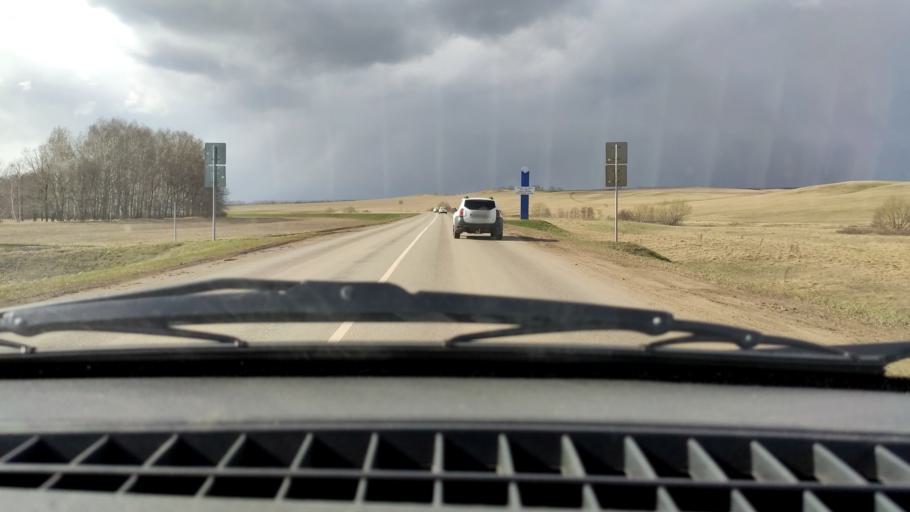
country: RU
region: Bashkortostan
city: Chekmagush
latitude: 55.1173
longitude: 54.7508
